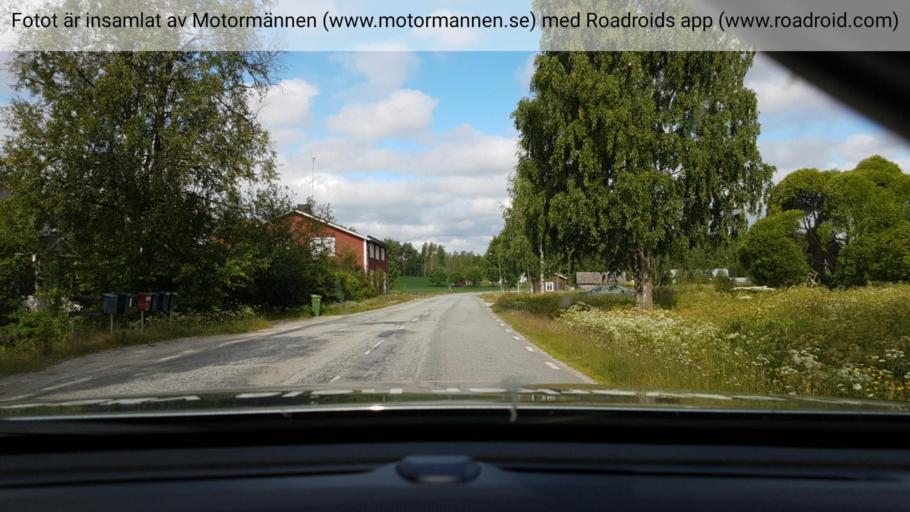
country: SE
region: Vaesterbotten
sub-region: Lycksele Kommun
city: Lycksele
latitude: 64.8151
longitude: 18.8881
